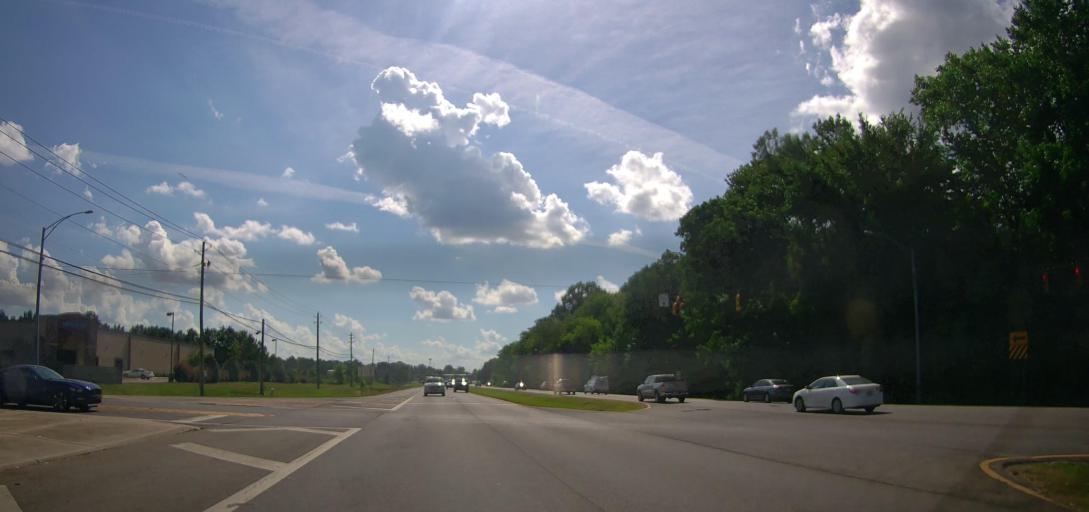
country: US
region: Alabama
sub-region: Tuscaloosa County
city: Northport
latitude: 33.2339
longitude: -87.6181
